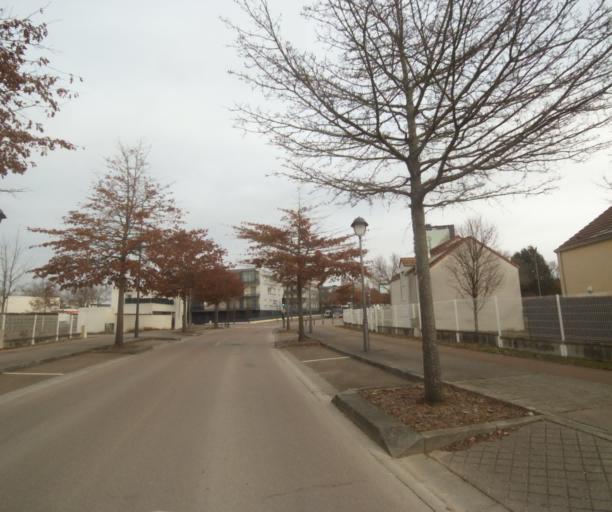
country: FR
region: Champagne-Ardenne
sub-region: Departement de la Haute-Marne
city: Bettancourt-la-Ferree
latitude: 48.6387
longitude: 4.9716
